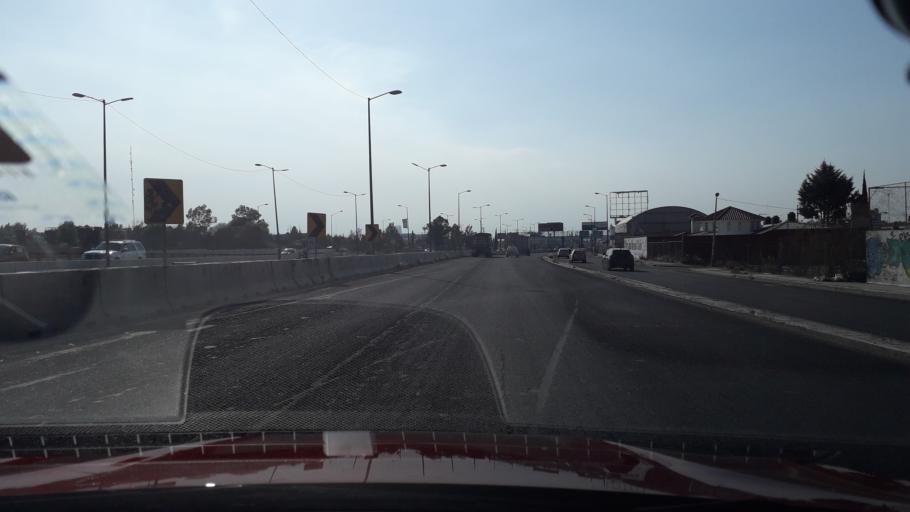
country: MX
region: Puebla
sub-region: Puebla
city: El Capulo (La Quebradora)
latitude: 18.9849
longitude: -98.2319
